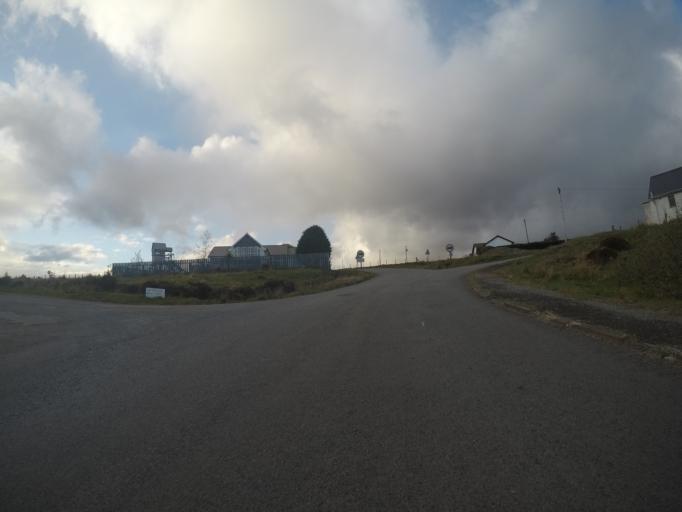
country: GB
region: Scotland
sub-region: Highland
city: Isle of Skye
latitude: 57.4537
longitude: -6.2979
